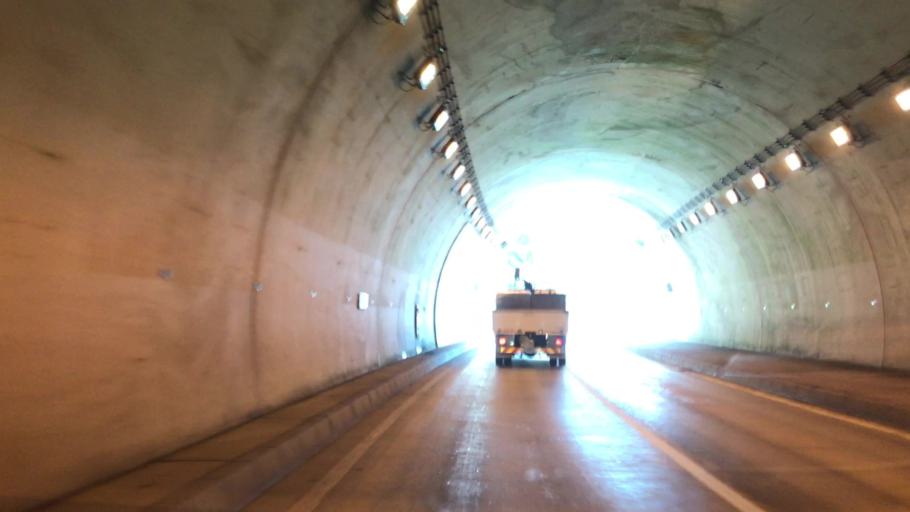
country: JP
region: Hokkaido
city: Iwanai
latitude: 43.1147
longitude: 140.4505
